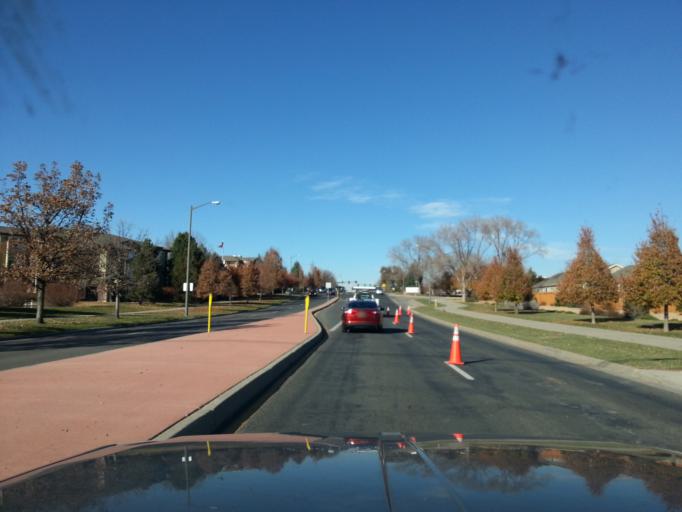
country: US
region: Colorado
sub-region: Larimer County
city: Loveland
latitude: 40.4045
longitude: -105.1104
